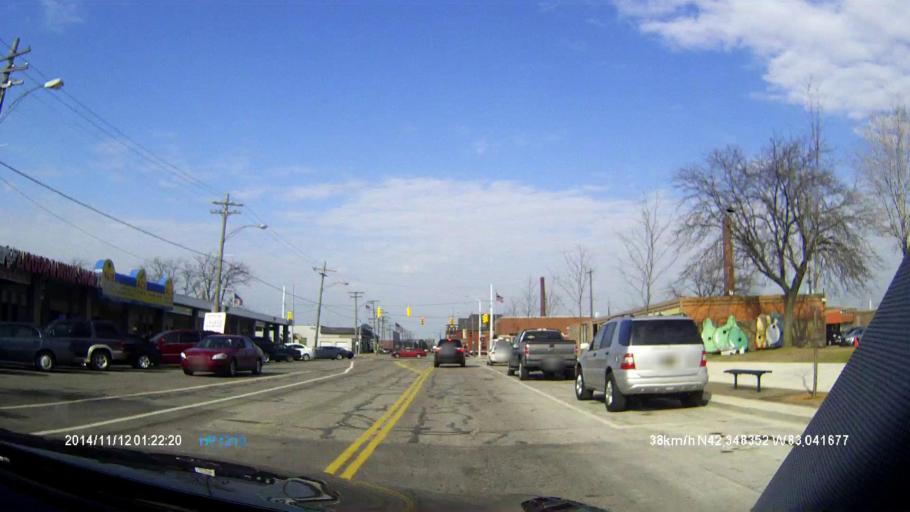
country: US
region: Michigan
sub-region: Wayne County
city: Detroit
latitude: 42.3484
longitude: -83.0417
